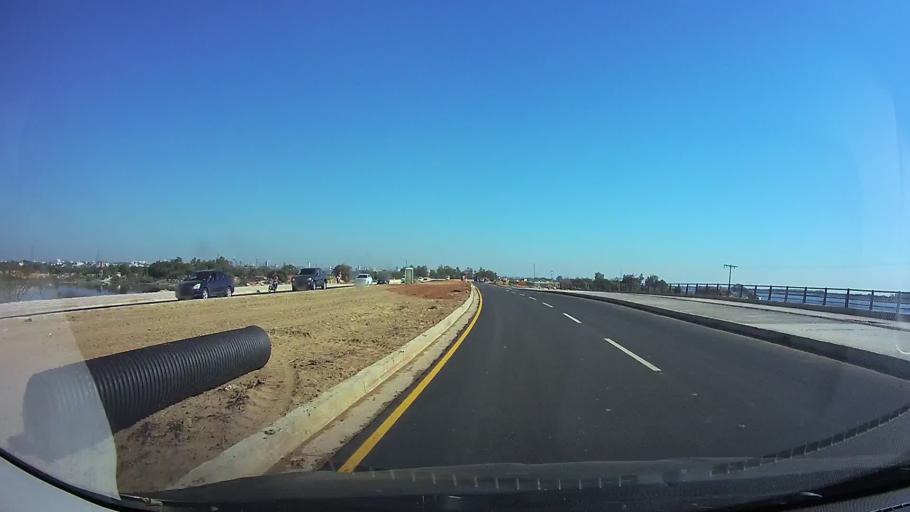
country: PY
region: Asuncion
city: Asuncion
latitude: -25.2468
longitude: -57.5975
